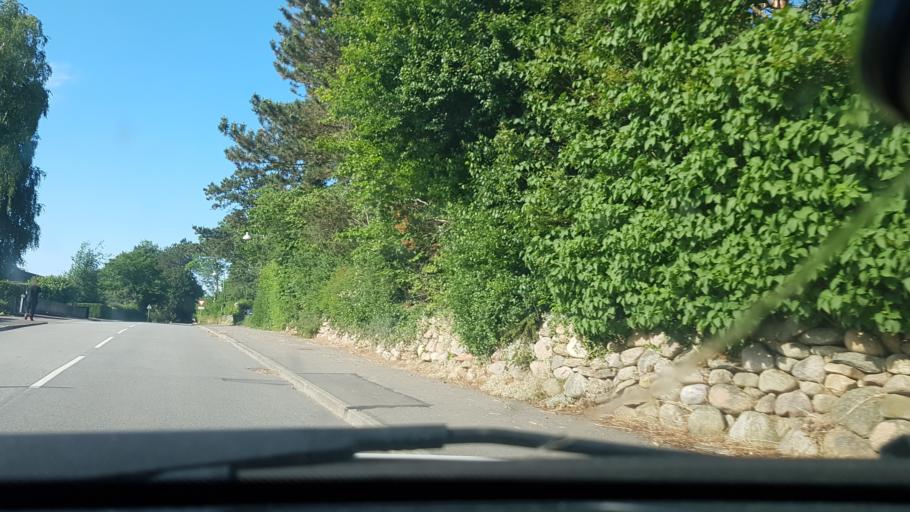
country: DK
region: Zealand
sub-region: Odsherred Kommune
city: Hojby
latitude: 55.8836
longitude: 11.6081
